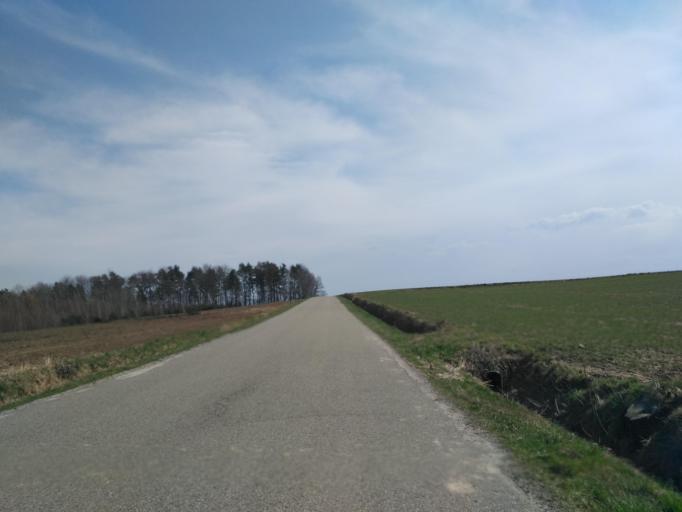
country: PL
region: Subcarpathian Voivodeship
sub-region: Powiat ropczycko-sedziszowski
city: Iwierzyce
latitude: 49.9730
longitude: 21.7518
